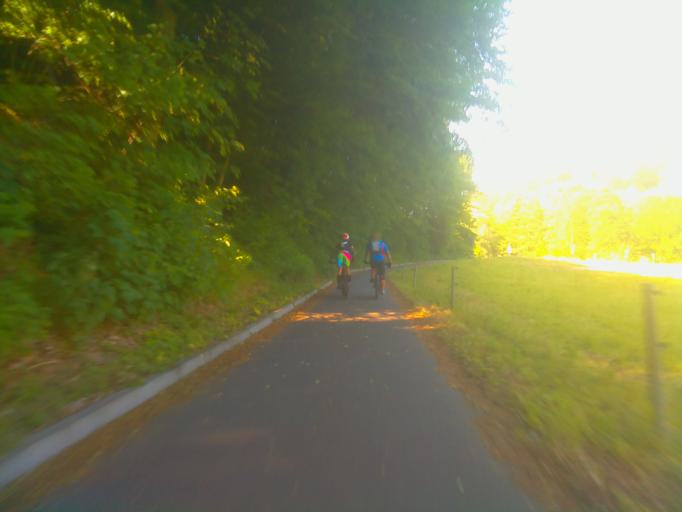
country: DE
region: Thuringia
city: Freienorla
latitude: 50.7591
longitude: 11.5428
